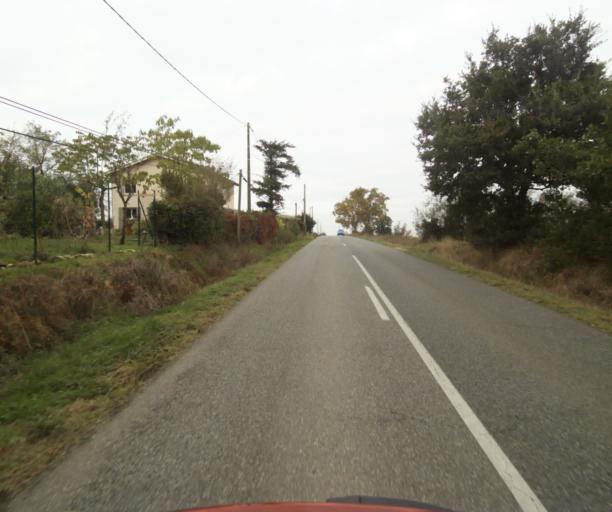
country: FR
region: Midi-Pyrenees
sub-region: Departement du Tarn-et-Garonne
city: Verdun-sur-Garonne
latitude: 43.8084
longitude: 1.2052
